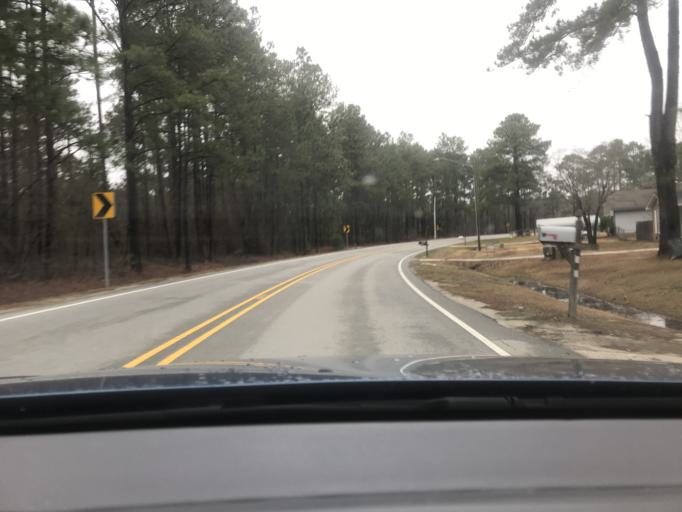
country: US
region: North Carolina
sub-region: Hoke County
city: Rockfish
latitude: 35.0252
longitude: -79.0120
